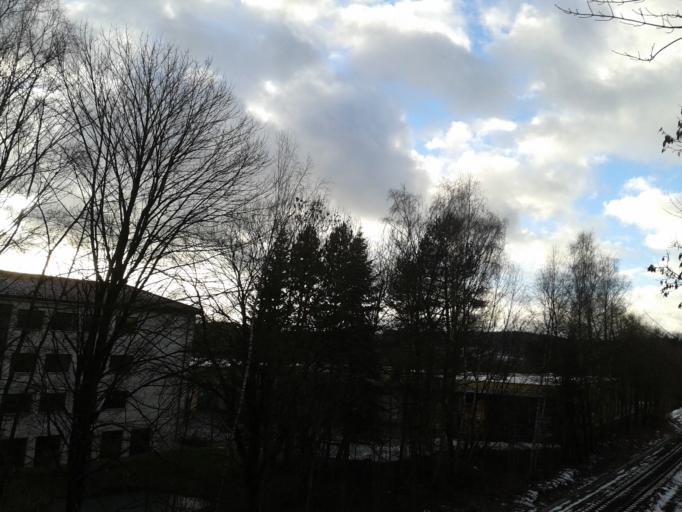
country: DE
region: Bavaria
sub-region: Upper Franconia
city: Marktschorgast
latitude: 50.0900
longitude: 11.6521
